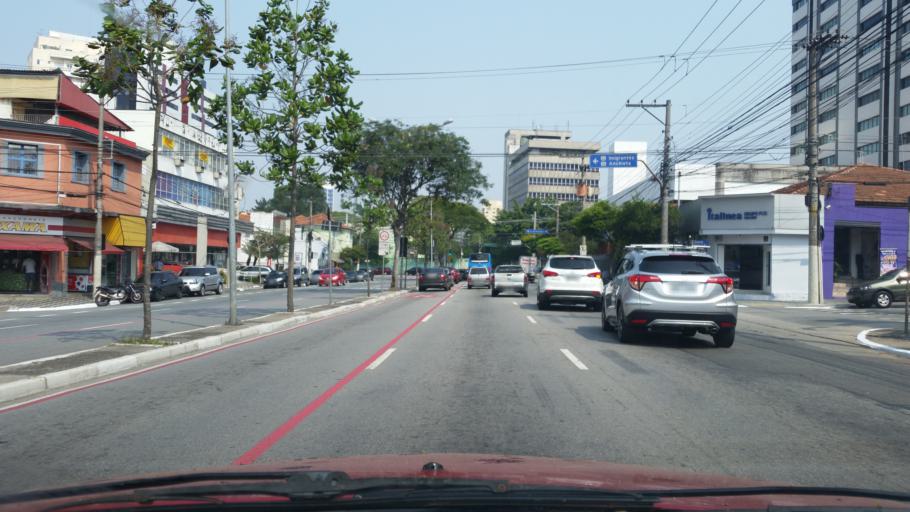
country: BR
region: Sao Paulo
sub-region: Diadema
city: Diadema
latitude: -23.6271
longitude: -46.6447
